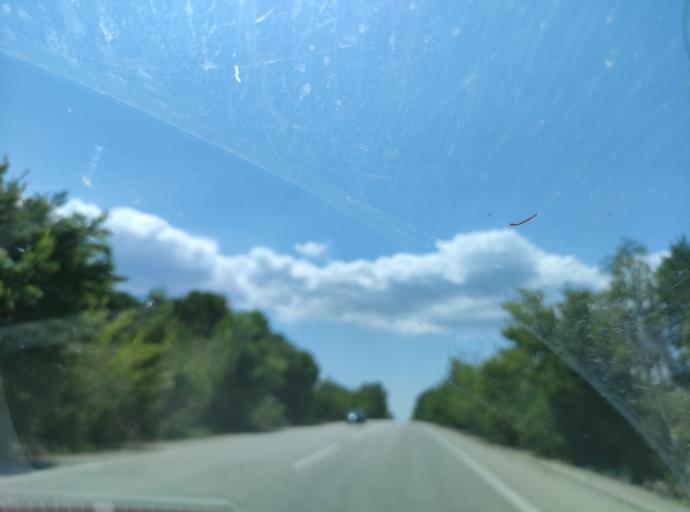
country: GR
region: East Macedonia and Thrace
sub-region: Nomos Dramas
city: Fotolivos
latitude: 40.9908
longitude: 24.0616
